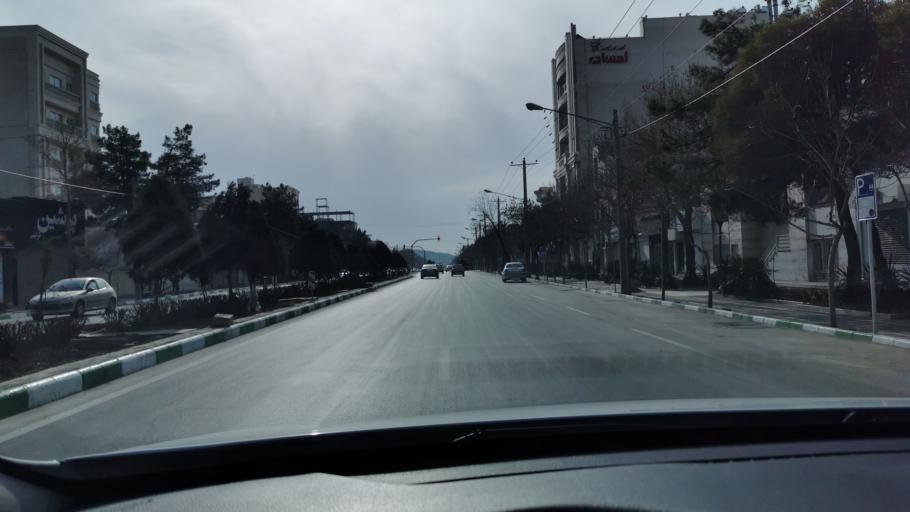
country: IR
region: Razavi Khorasan
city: Mashhad
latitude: 36.2900
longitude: 59.5394
